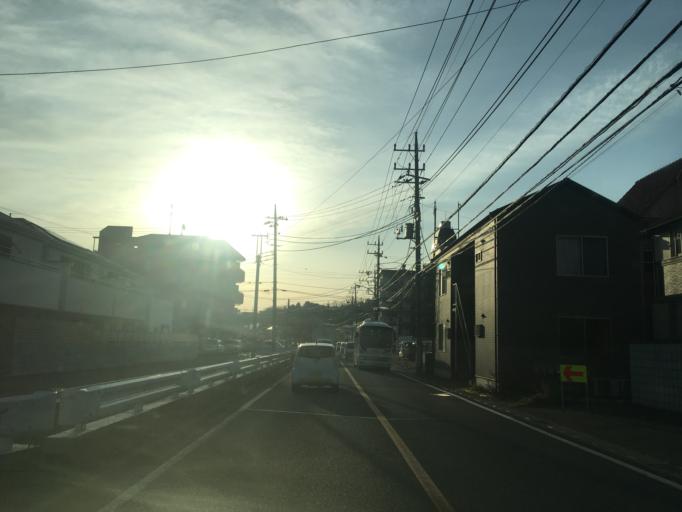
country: JP
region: Tokyo
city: Hino
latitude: 35.6578
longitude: 139.4261
